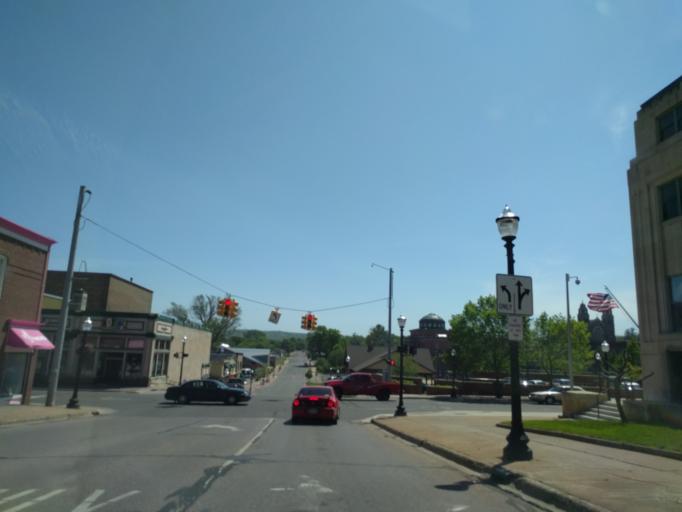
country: US
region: Michigan
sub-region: Marquette County
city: Marquette
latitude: 46.5439
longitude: -87.3954
